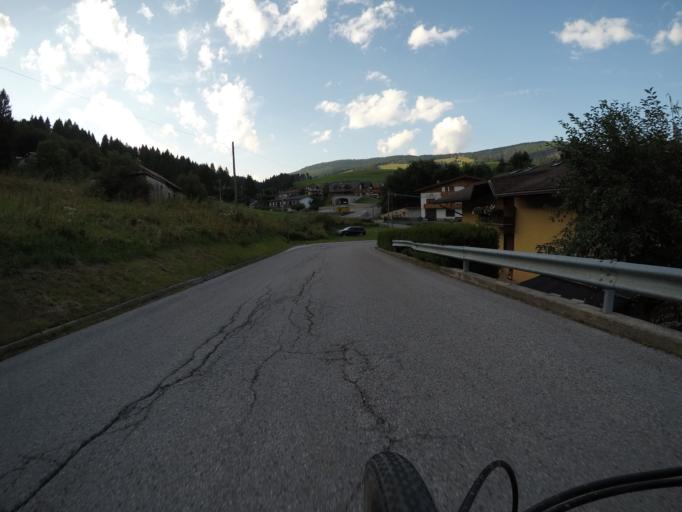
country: IT
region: Veneto
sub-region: Provincia di Vicenza
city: Gallio
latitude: 45.8931
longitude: 11.5414
